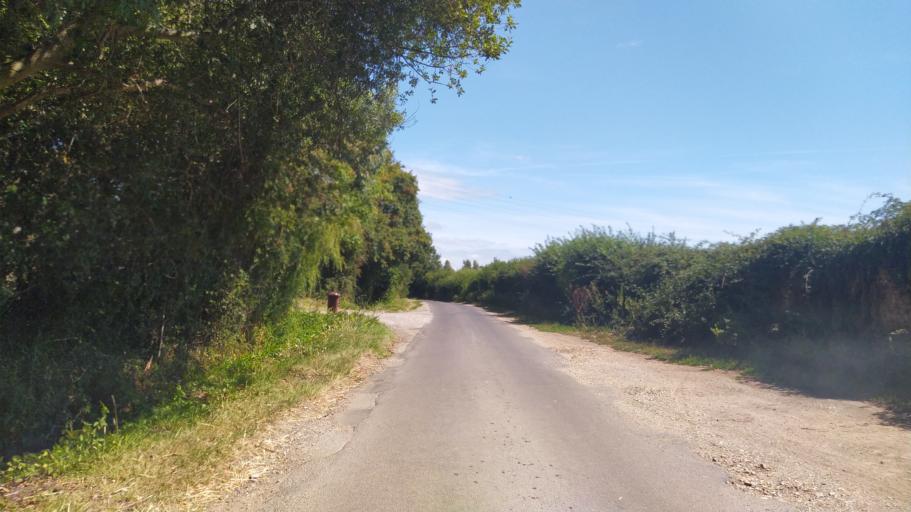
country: GB
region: England
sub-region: West Sussex
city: Chichester
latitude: 50.8076
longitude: -0.7594
